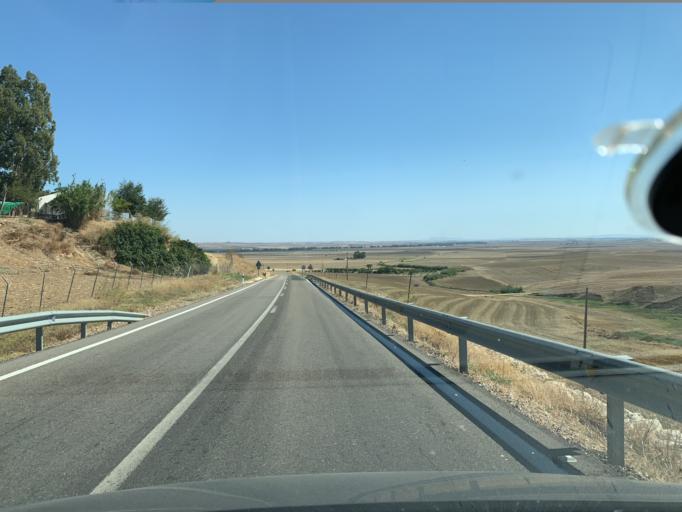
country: ES
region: Andalusia
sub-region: Provincia de Sevilla
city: Carmona
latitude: 37.4647
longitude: -5.6351
